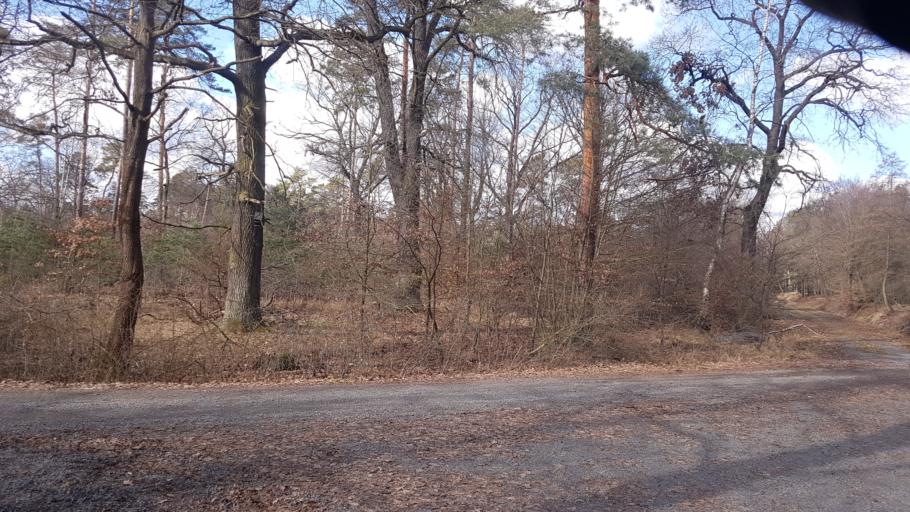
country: DE
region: Brandenburg
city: Falkenberg
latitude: 51.6082
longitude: 13.2175
